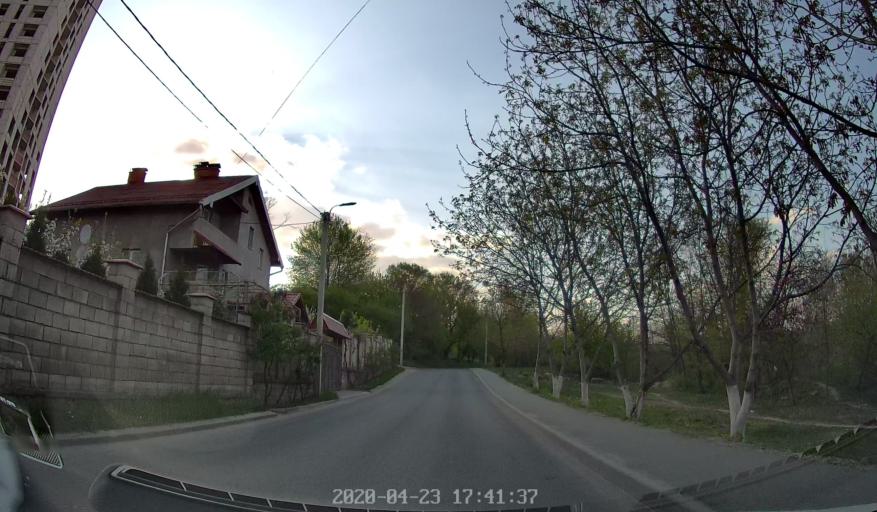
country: MD
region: Chisinau
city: Chisinau
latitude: 46.9876
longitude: 28.8372
